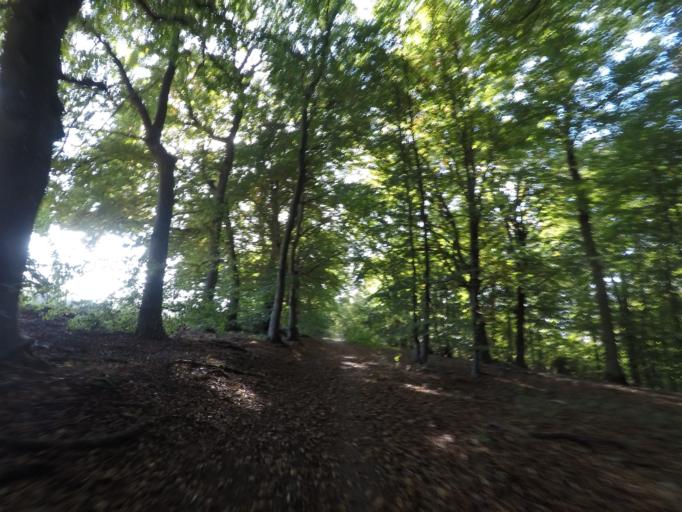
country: LU
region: Luxembourg
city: Itzig
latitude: 49.5928
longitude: 6.1641
